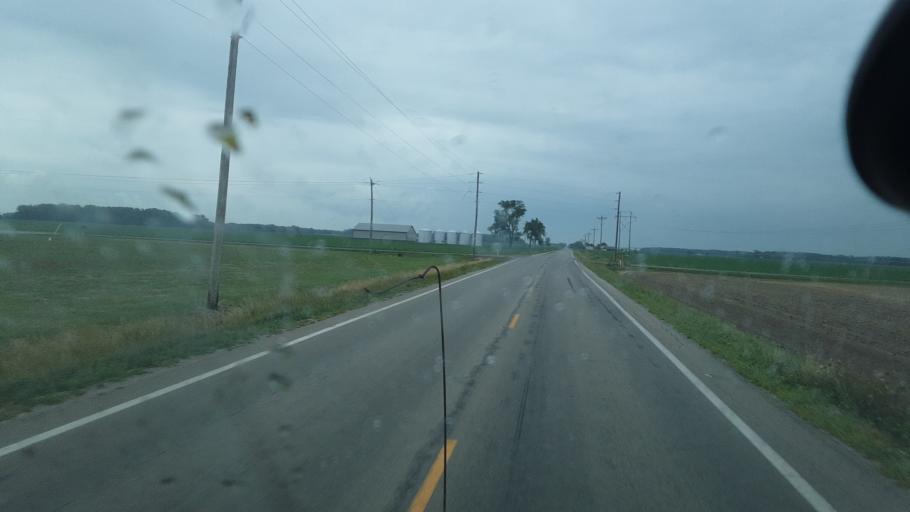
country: US
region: Ohio
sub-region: Defiance County
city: Hicksville
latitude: 41.2961
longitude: -84.6911
